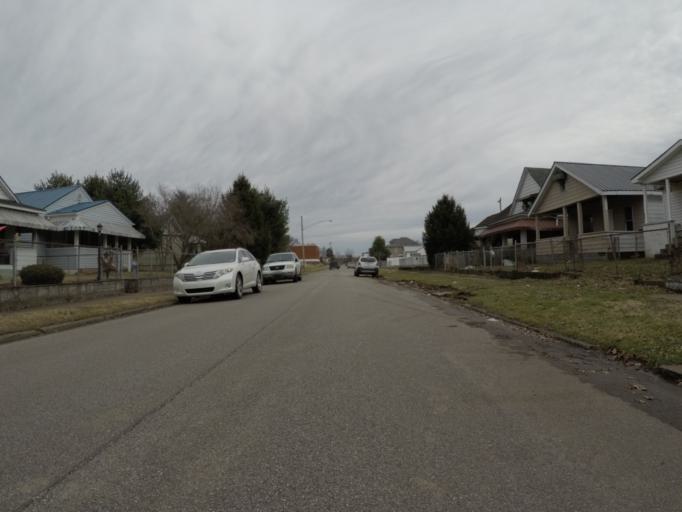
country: US
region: West Virginia
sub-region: Cabell County
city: Huntington
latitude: 38.4077
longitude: -82.4889
